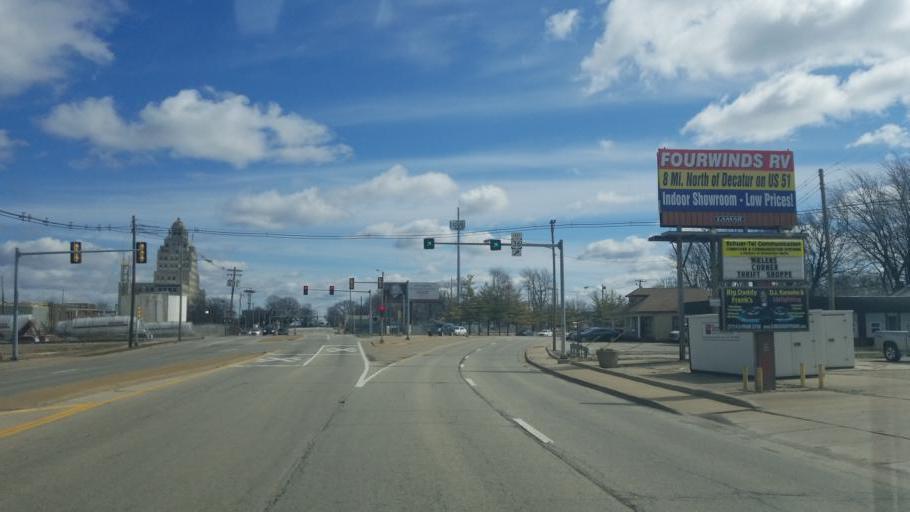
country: US
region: Illinois
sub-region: Macon County
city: Decatur
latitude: 39.8464
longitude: -88.9301
